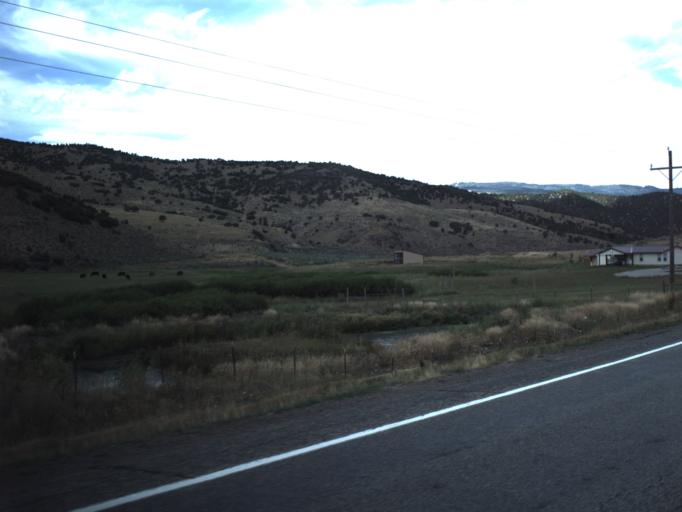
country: US
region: Utah
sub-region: Utah County
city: Woodland Hills
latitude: 39.8634
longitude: -111.5294
